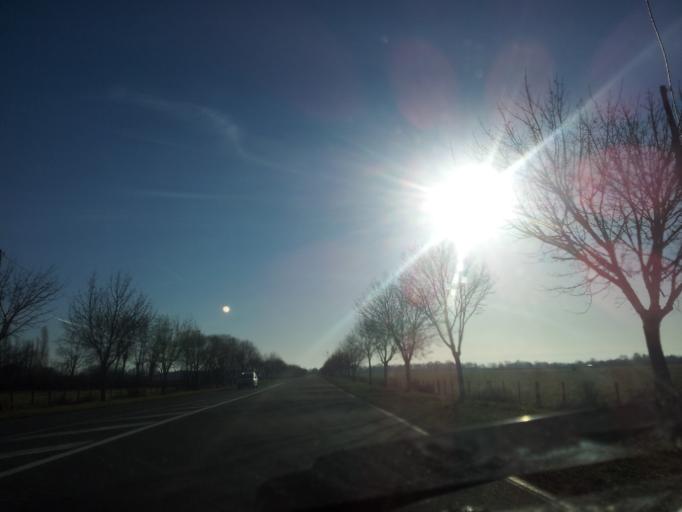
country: FR
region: Auvergne
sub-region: Departement de l'Allier
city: Chantelle
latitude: 46.3161
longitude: 3.1848
